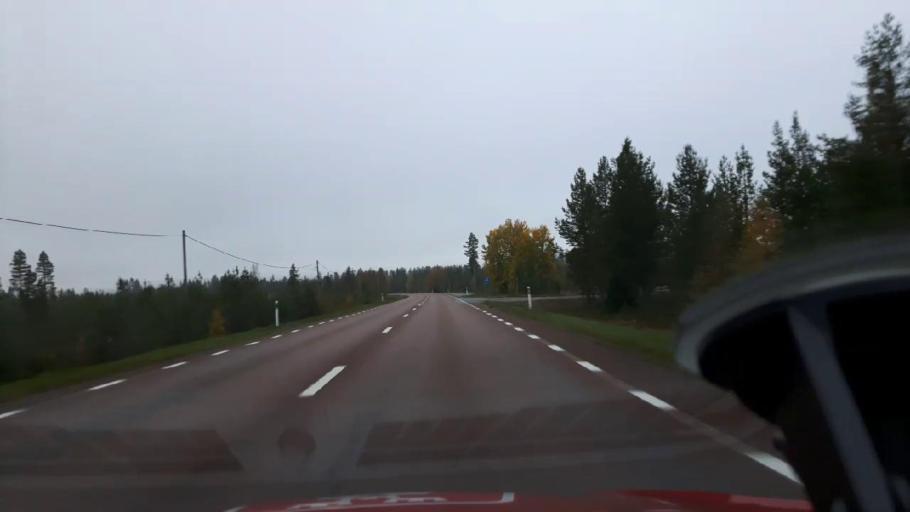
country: SE
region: Jaemtland
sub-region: Bergs Kommun
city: Hoverberg
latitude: 62.5125
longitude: 14.4498
